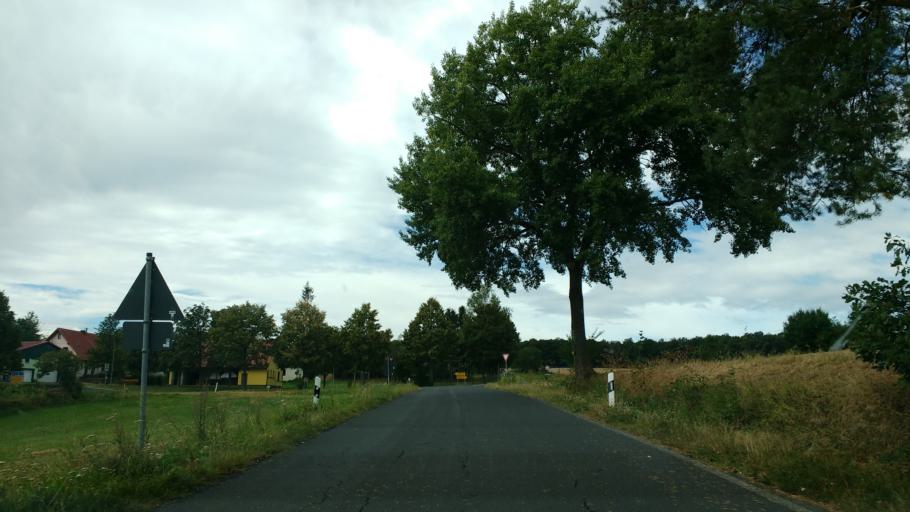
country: DE
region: Bavaria
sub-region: Regierungsbezirk Unterfranken
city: Geiselwind
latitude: 49.7954
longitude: 10.5142
